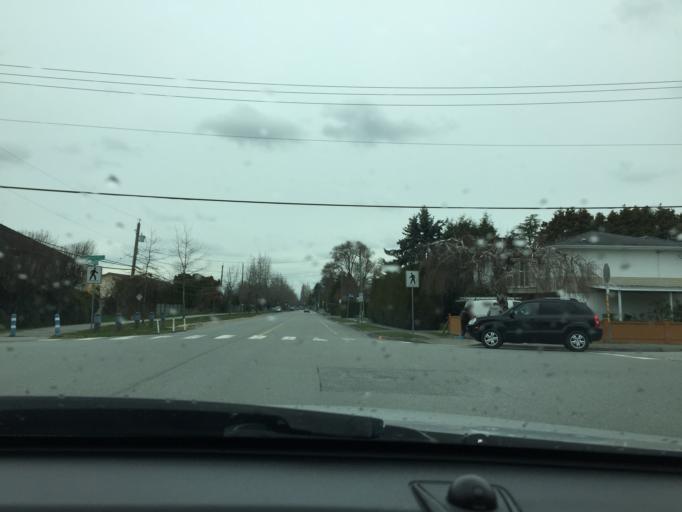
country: CA
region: British Columbia
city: Richmond
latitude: 49.1433
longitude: -123.1252
